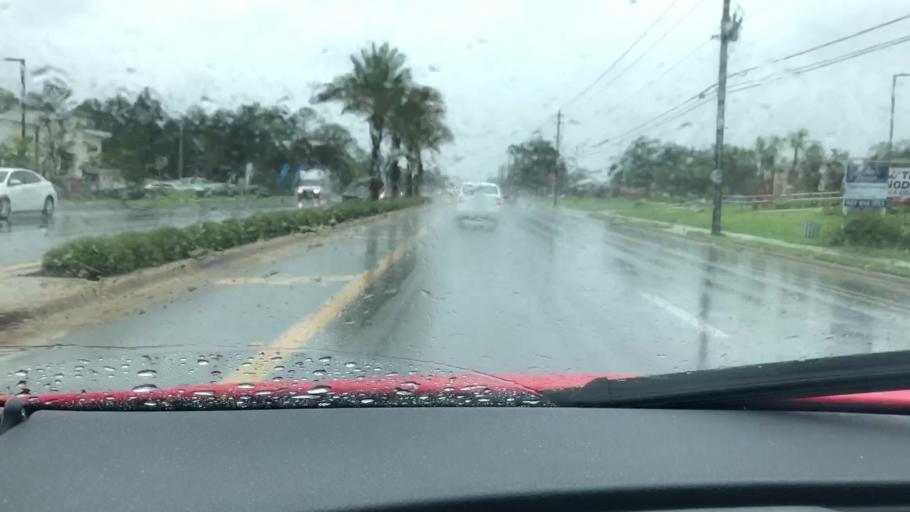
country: US
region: Florida
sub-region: Volusia County
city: South Daytona
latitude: 29.1731
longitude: -81.0340
